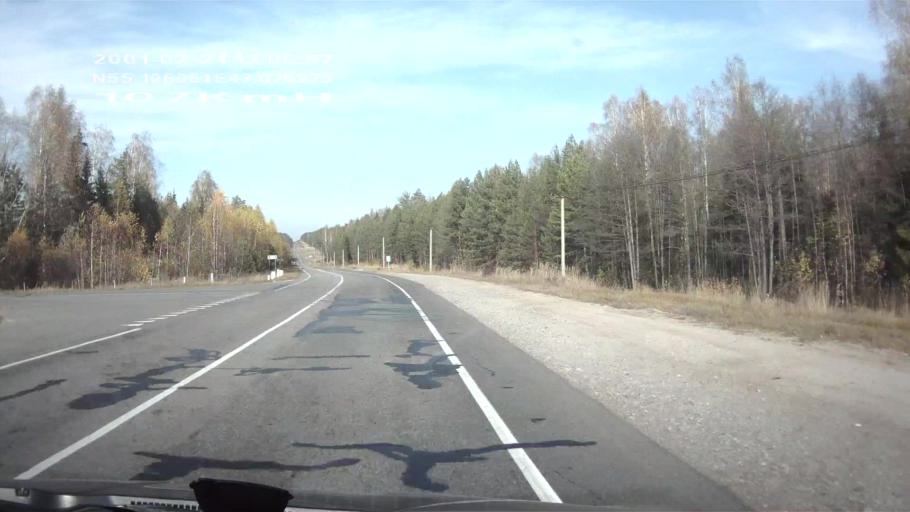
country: RU
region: Chuvashia
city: Buinsk
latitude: 55.1959
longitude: 47.0769
